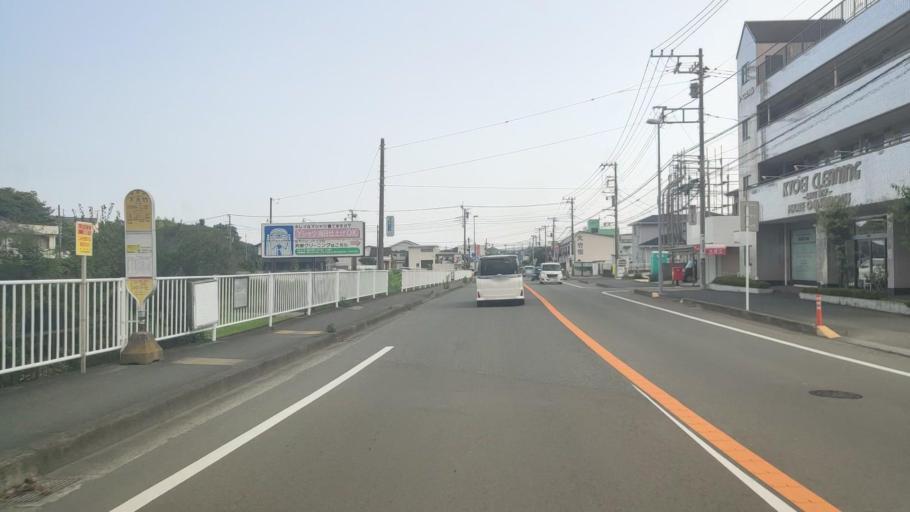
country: JP
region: Kanagawa
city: Isehara
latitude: 35.3867
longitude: 139.3162
